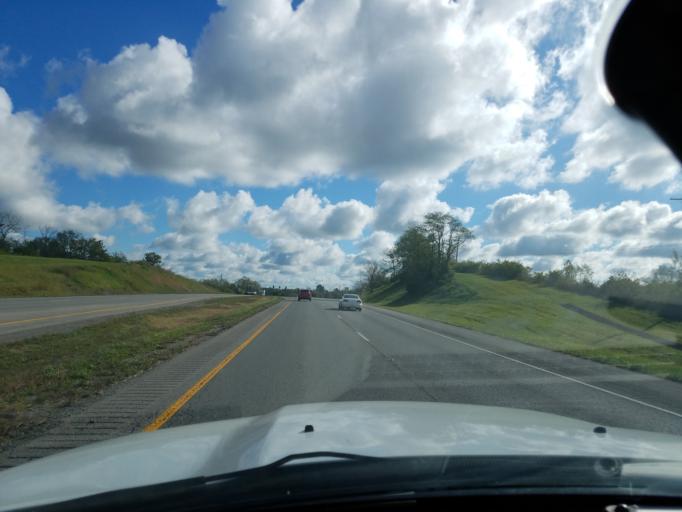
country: US
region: Kentucky
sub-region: Boyle County
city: Danville
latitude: 37.6204
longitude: -84.7566
